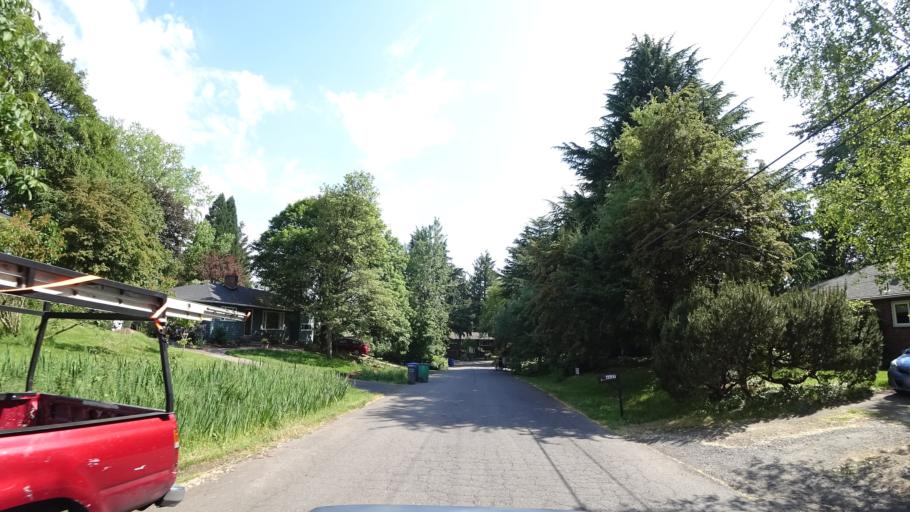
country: US
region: Oregon
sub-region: Washington County
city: Metzger
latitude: 45.4536
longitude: -122.7381
